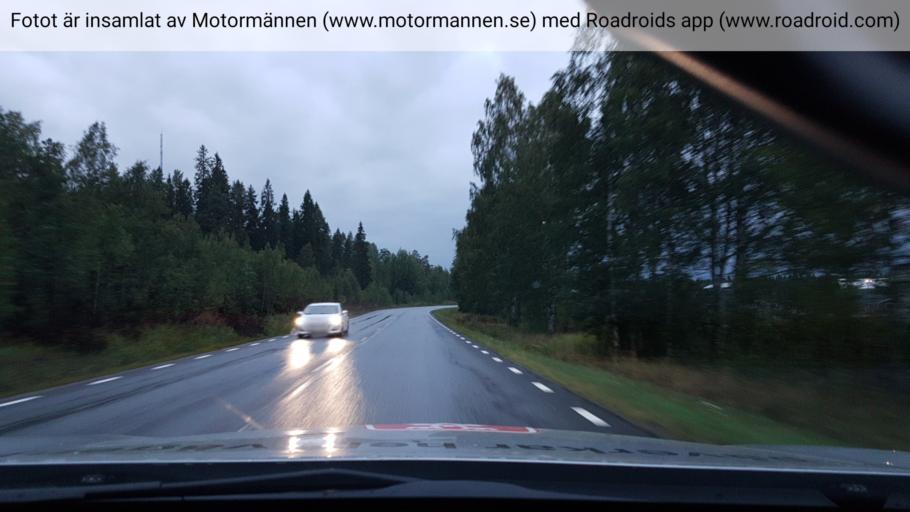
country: SE
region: Vaesterbotten
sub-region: Umea Kommun
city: Ersmark
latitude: 63.8653
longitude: 20.3004
